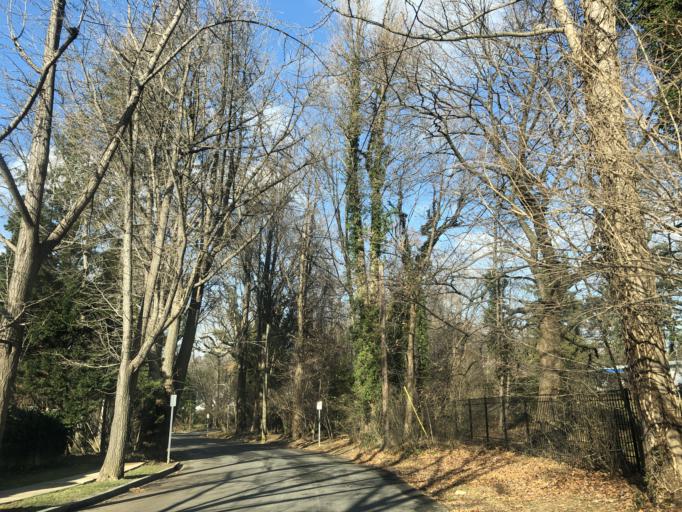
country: US
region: Pennsylvania
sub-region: Montgomery County
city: Bala-Cynwyd
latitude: 40.0053
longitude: -75.2243
